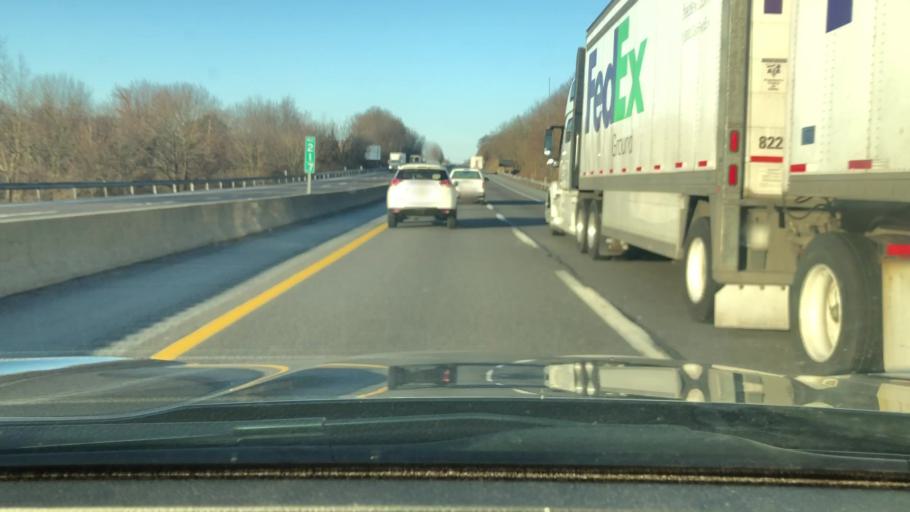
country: US
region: Pennsylvania
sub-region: Schuylkill County
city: Lake Wynonah
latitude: 40.5108
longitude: -76.1338
